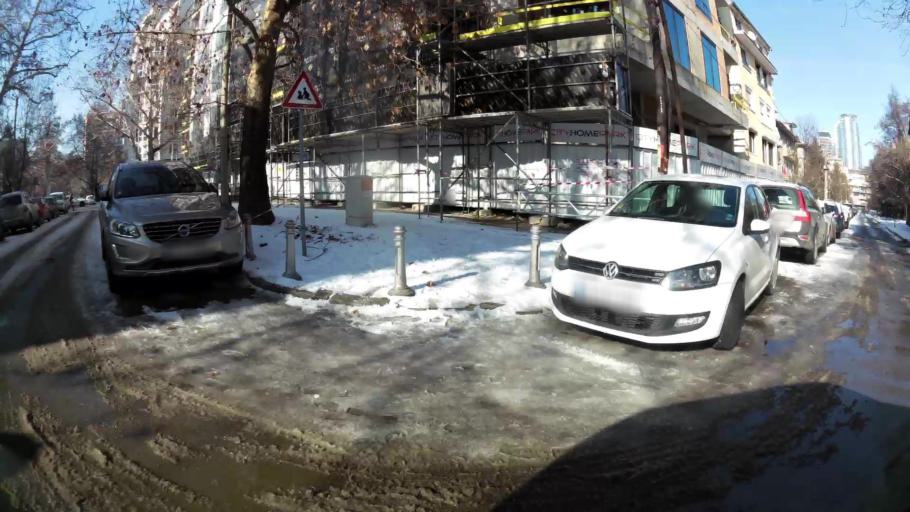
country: BG
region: Sofia-Capital
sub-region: Stolichna Obshtina
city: Sofia
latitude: 42.6774
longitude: 23.3107
